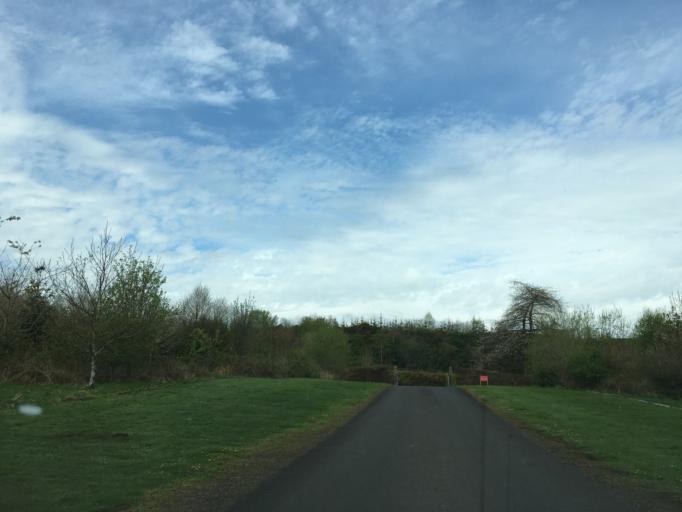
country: GB
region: Scotland
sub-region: Argyll and Bute
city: Rothesay
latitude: 55.8014
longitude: -5.0262
